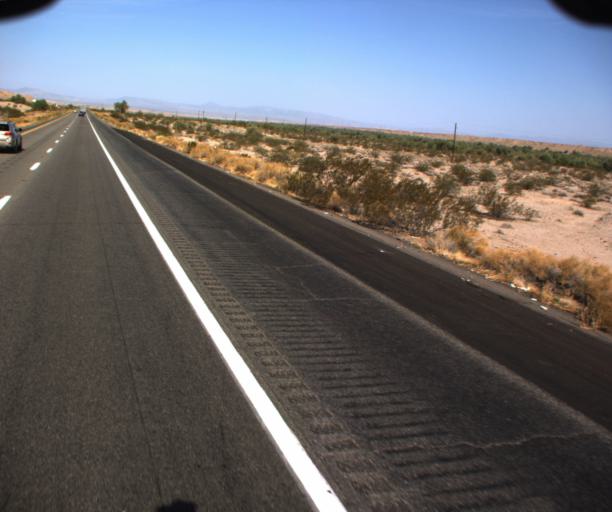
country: US
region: Arizona
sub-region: Mohave County
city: Desert Hills
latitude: 34.7288
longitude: -114.3493
